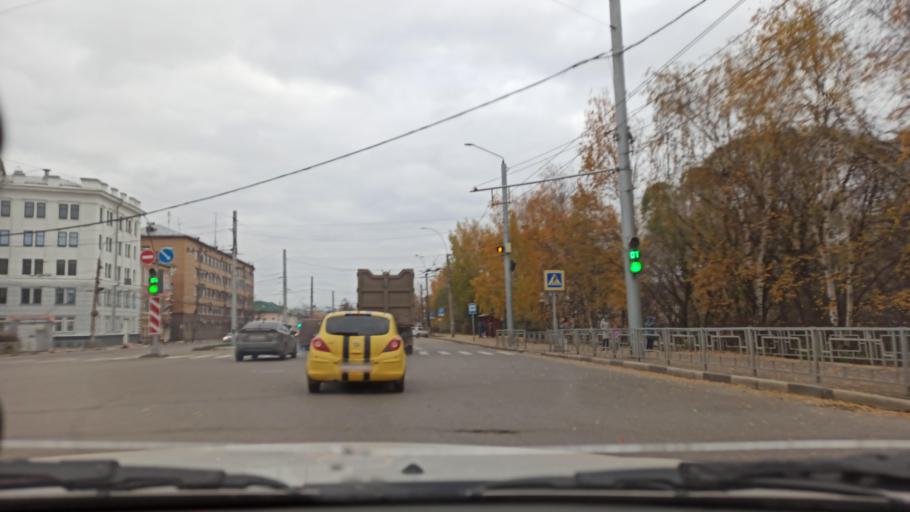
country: RU
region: Vologda
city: Vologda
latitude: 59.2179
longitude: 39.8836
